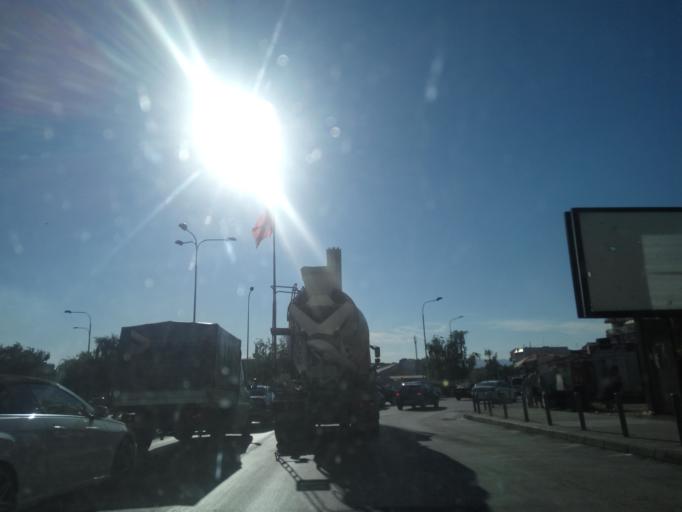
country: XK
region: Pristina
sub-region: Komuna e Prishtines
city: Pristina
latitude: 42.6474
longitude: 21.1584
